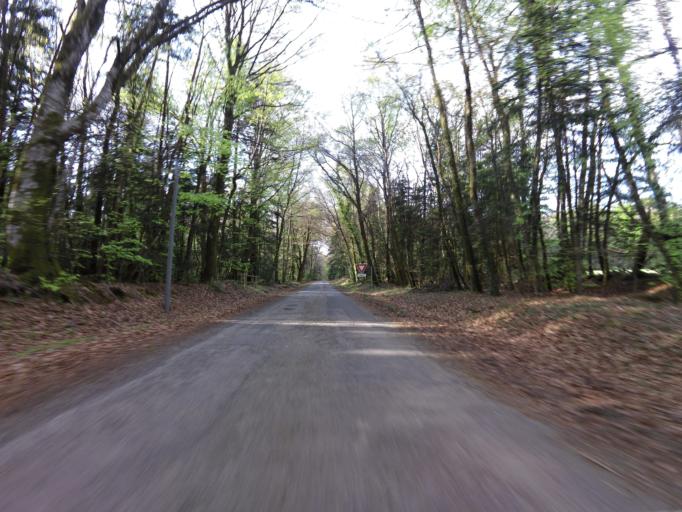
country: FR
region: Brittany
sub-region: Departement du Morbihan
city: Pluherlin
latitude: 47.7229
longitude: -2.3703
